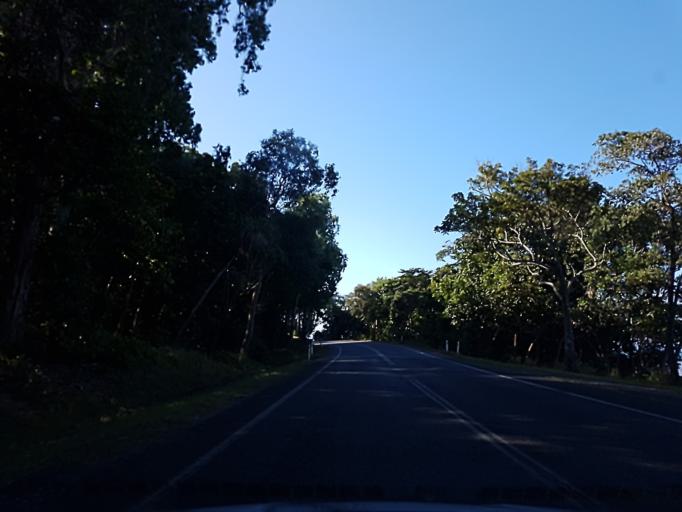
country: AU
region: Queensland
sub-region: Cairns
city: Port Douglas
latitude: -16.3682
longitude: 145.4121
